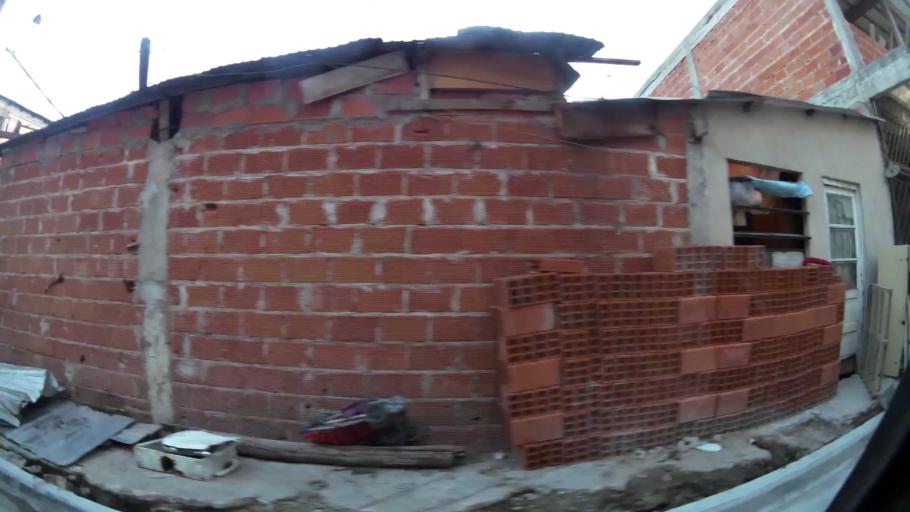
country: AR
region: Buenos Aires
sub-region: Partido de Avellaneda
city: Avellaneda
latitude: -34.6796
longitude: -58.3273
